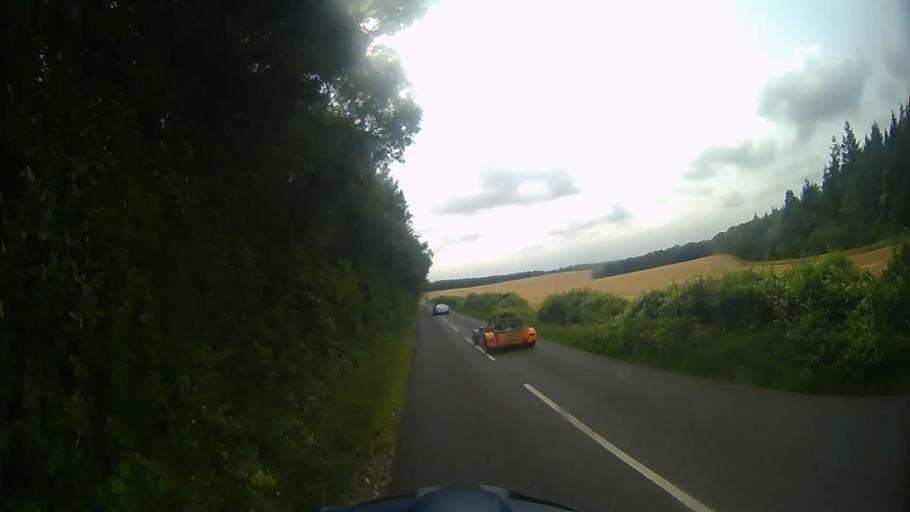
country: GB
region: England
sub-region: Hampshire
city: Overton
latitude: 51.2849
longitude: -1.2821
